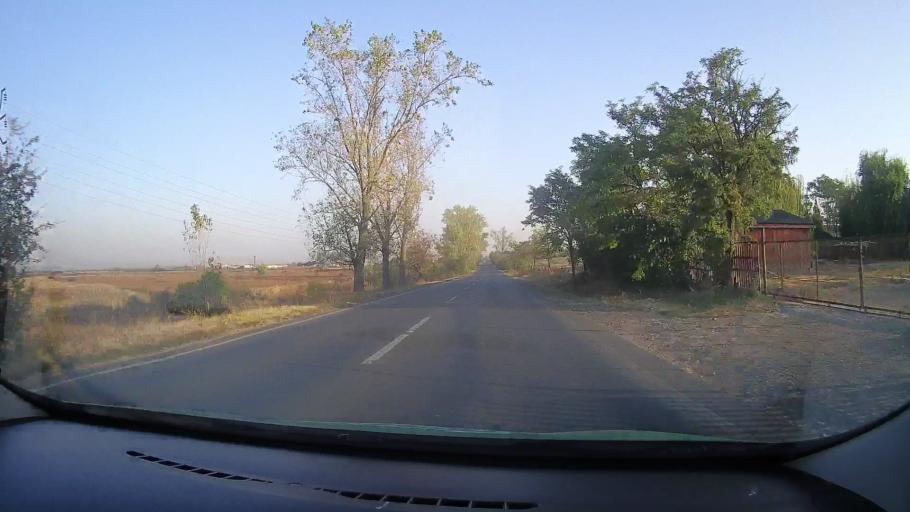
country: RO
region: Arad
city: Arad
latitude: 46.2221
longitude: 21.3205
